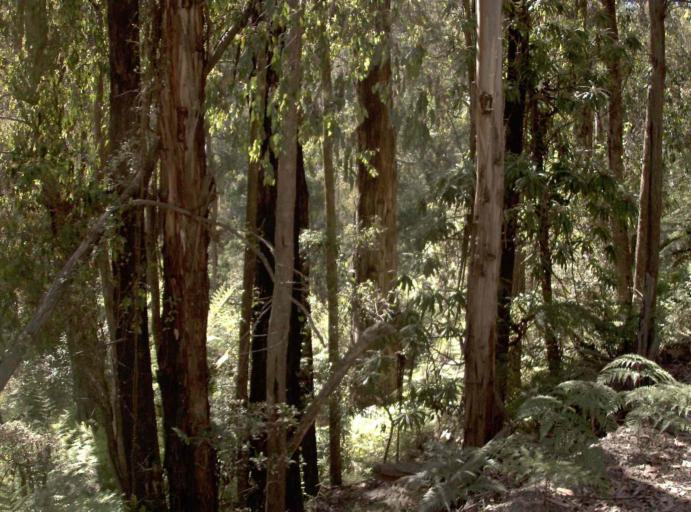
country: AU
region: New South Wales
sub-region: Bombala
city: Bombala
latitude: -37.2480
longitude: 148.7490
